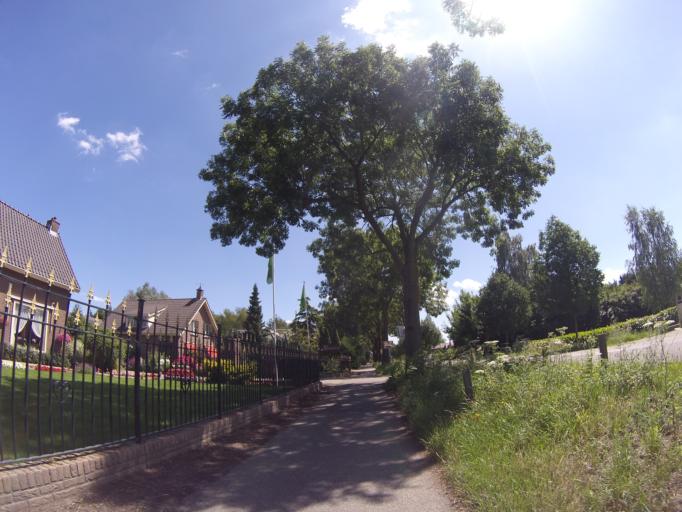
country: NL
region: Utrecht
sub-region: Stichtse Vecht
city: Maarssen
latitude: 52.1341
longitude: 5.0915
